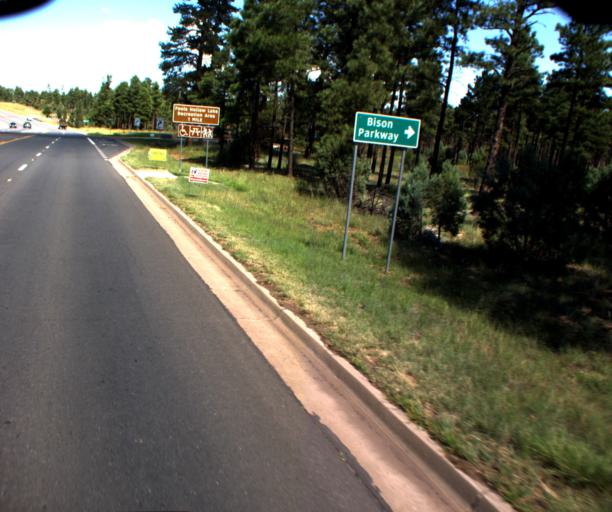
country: US
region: Arizona
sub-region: Navajo County
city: Show Low
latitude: 34.2477
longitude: -110.0718
